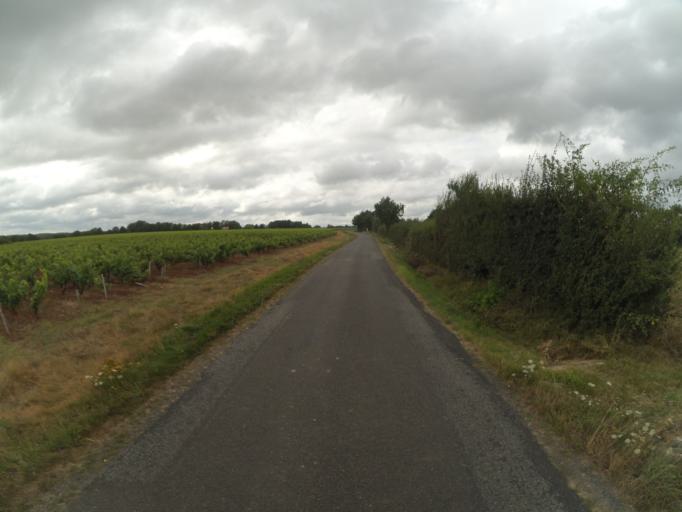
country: FR
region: Pays de la Loire
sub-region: Departement de la Vendee
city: Saint-Philbert-de-Bouaine
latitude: 47.0034
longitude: -1.5282
